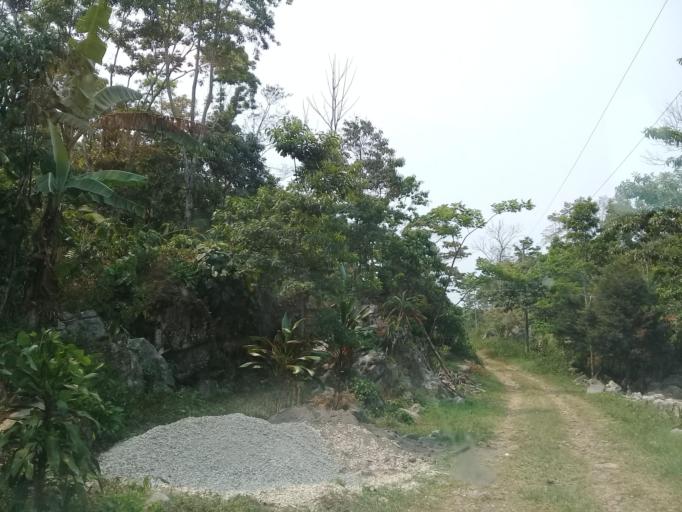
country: MX
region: Veracruz
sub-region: Tezonapa
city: Laguna Chica (Pueblo Nuevo)
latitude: 18.5871
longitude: -96.7464
